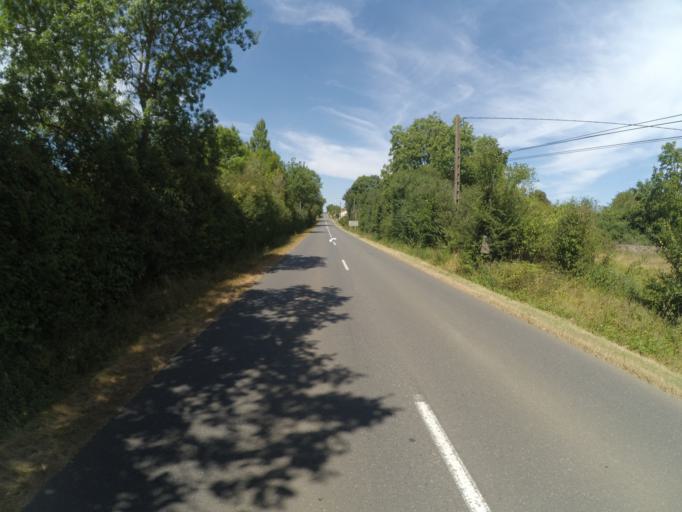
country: FR
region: Poitou-Charentes
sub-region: Departement de la Vienne
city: Usson-du-Poitou
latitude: 46.2677
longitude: 0.5203
